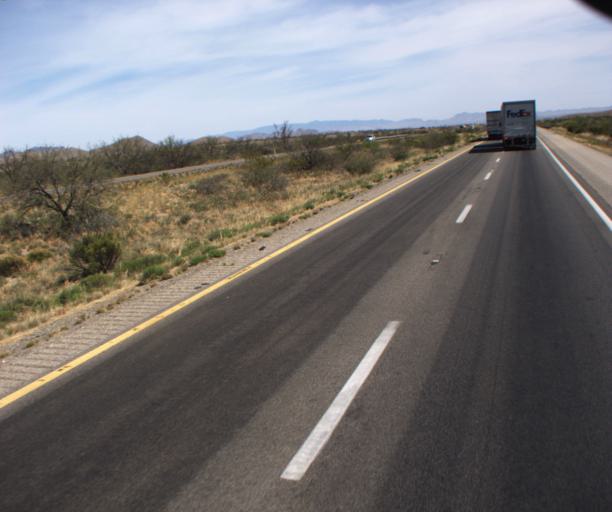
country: US
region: Arizona
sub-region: Cochise County
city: Willcox
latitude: 32.1264
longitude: -110.0118
